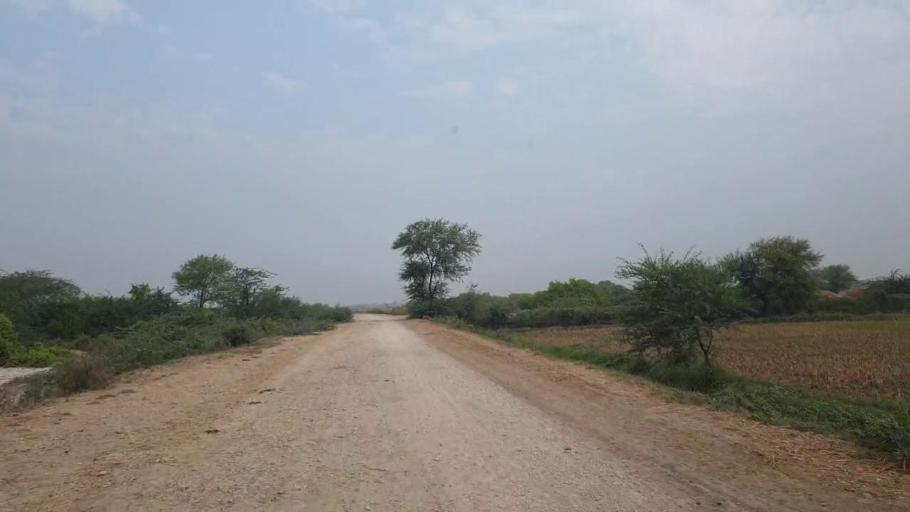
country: PK
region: Sindh
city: Tando Bago
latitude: 24.7978
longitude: 68.8757
